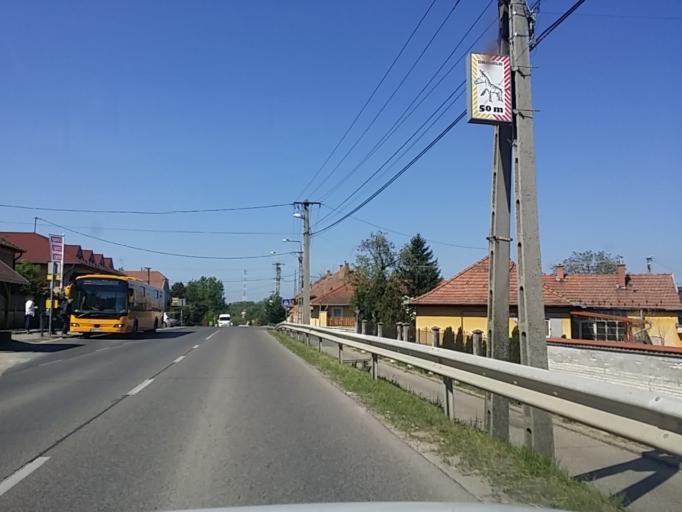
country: HU
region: Pest
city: Mogyorod
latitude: 47.6020
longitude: 19.2473
